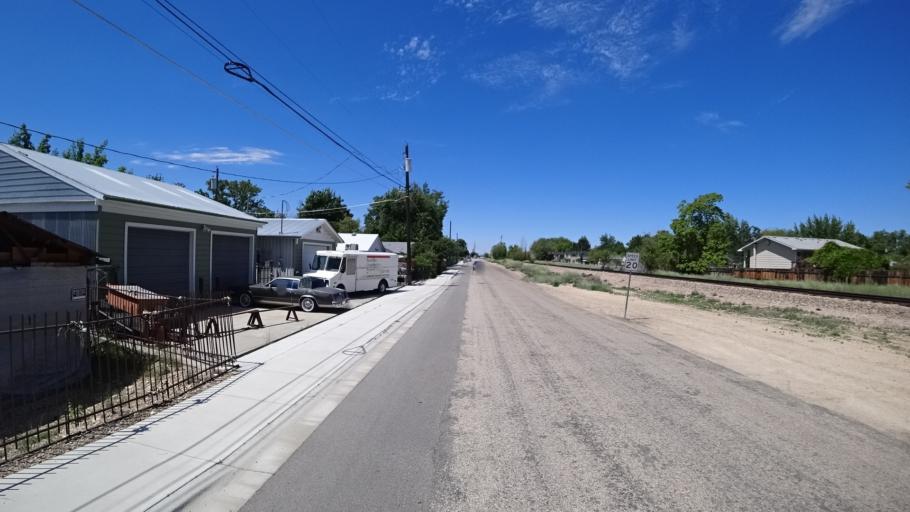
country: US
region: Idaho
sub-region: Ada County
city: Garden City
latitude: 43.6043
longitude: -116.2389
